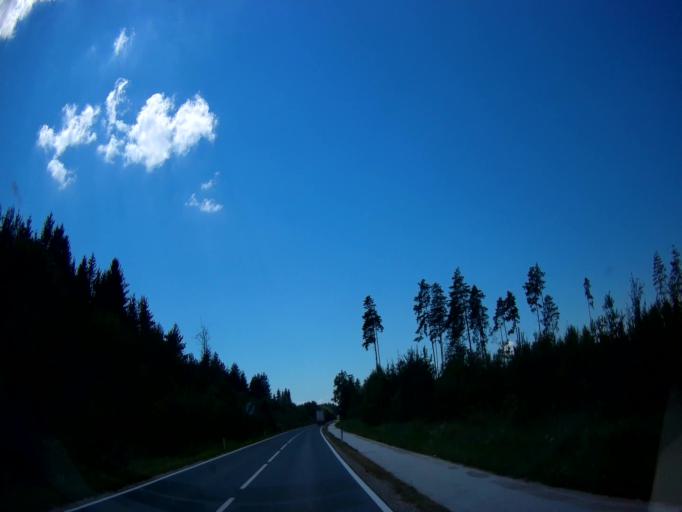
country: AT
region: Carinthia
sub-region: Politischer Bezirk Volkermarkt
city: Eberndorf
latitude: 46.6097
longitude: 14.6824
